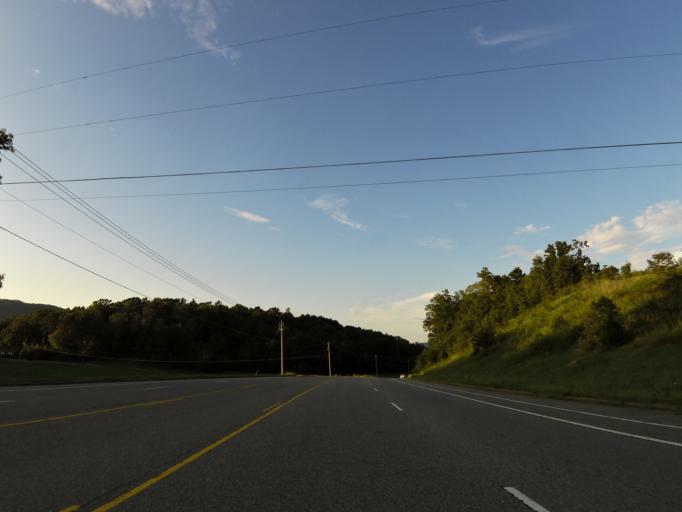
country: US
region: Tennessee
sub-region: Grainger County
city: Blaine
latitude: 36.1419
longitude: -83.7140
